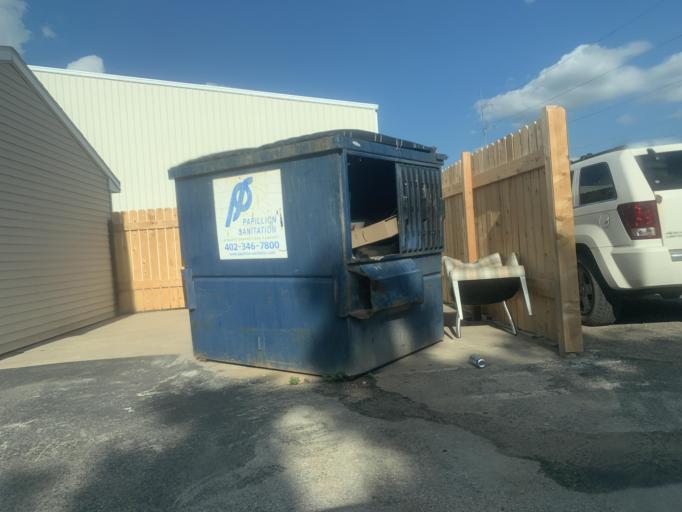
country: US
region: Nebraska
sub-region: Sarpy County
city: Chalco
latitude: 41.1767
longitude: -96.1457
